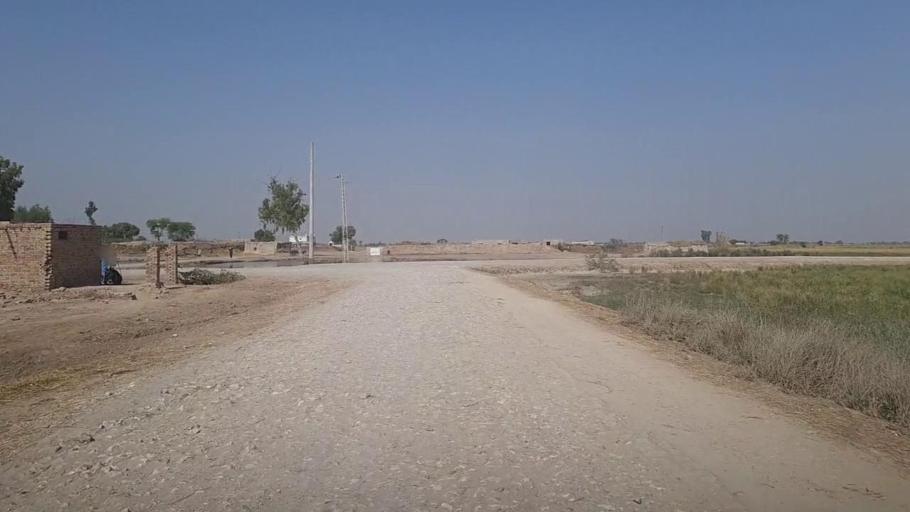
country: PK
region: Sindh
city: Kandhkot
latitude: 28.3948
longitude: 69.3260
